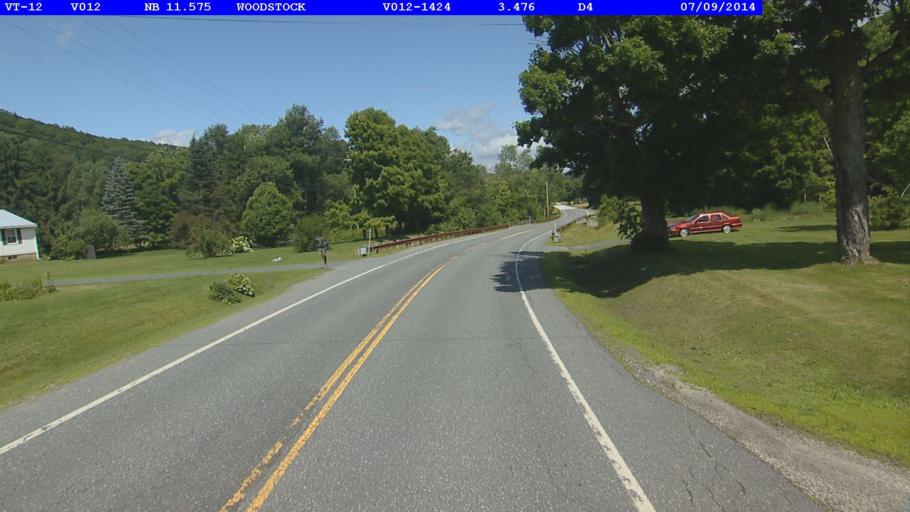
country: US
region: Vermont
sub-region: Windsor County
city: Woodstock
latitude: 43.6508
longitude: -72.5621
